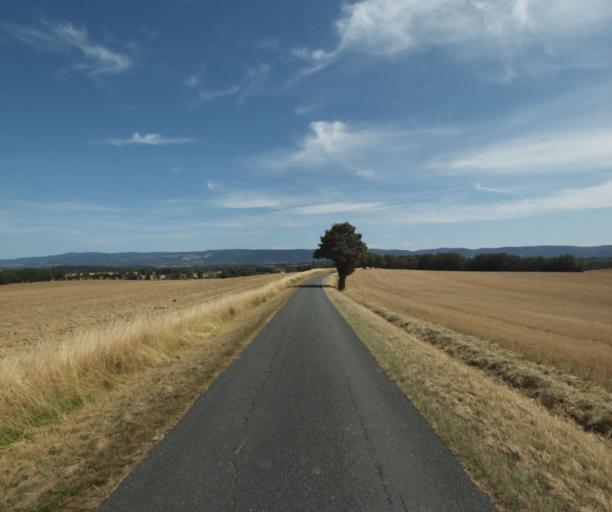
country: FR
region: Midi-Pyrenees
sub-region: Departement du Tarn
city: Puylaurens
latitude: 43.5303
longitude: 2.0211
